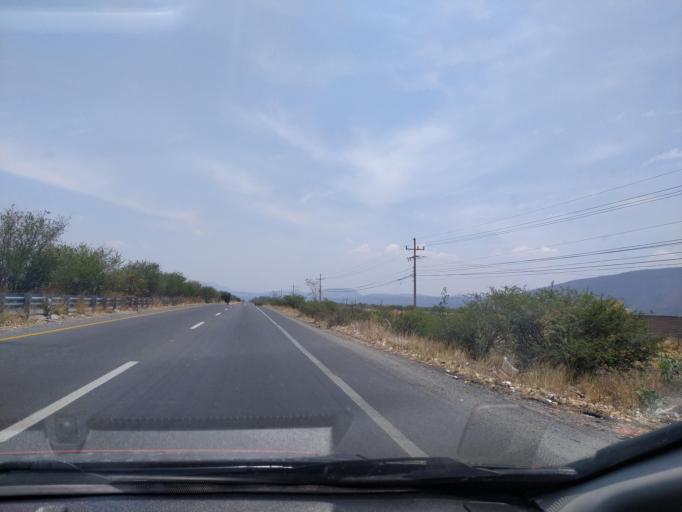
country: MX
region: Jalisco
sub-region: Acatlan de Juarez
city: Villa de los Ninos
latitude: 20.3523
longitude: -103.5915
